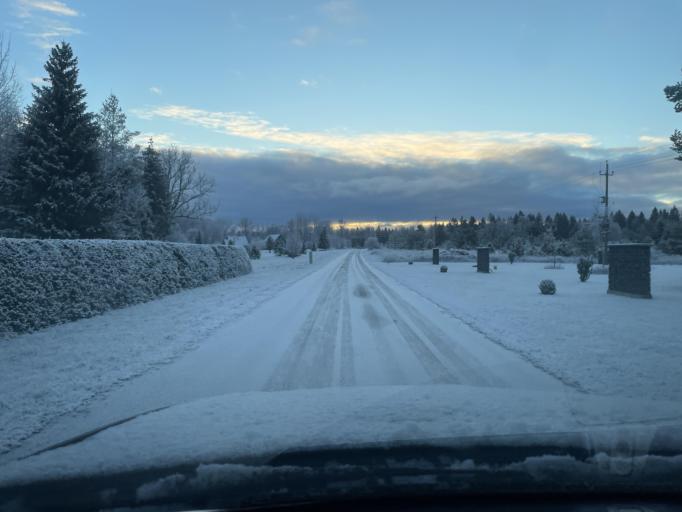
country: EE
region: Harju
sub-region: Keila linn
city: Keila
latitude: 59.3117
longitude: 24.2772
